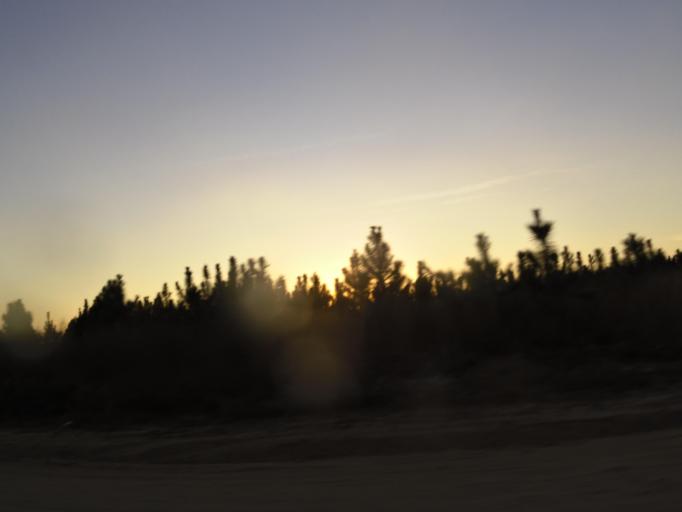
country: US
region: Florida
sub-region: Clay County
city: Green Cove Springs
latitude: 29.9138
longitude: -81.7806
